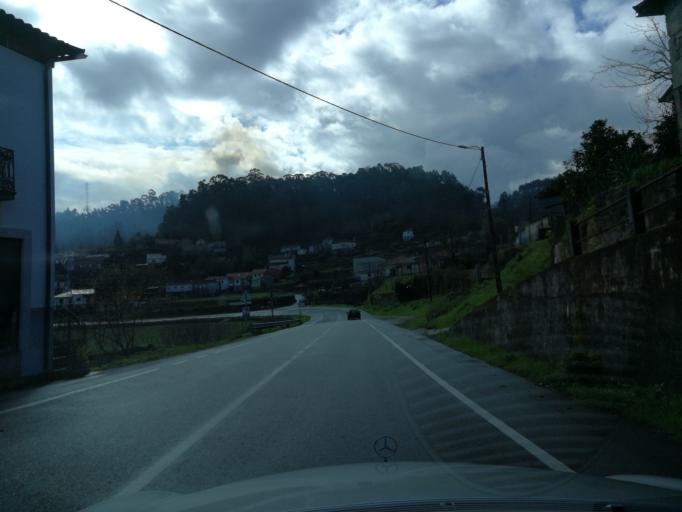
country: PT
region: Viana do Castelo
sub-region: Ponte da Barca
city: Ponte da Barca
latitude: 41.8100
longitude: -8.3835
